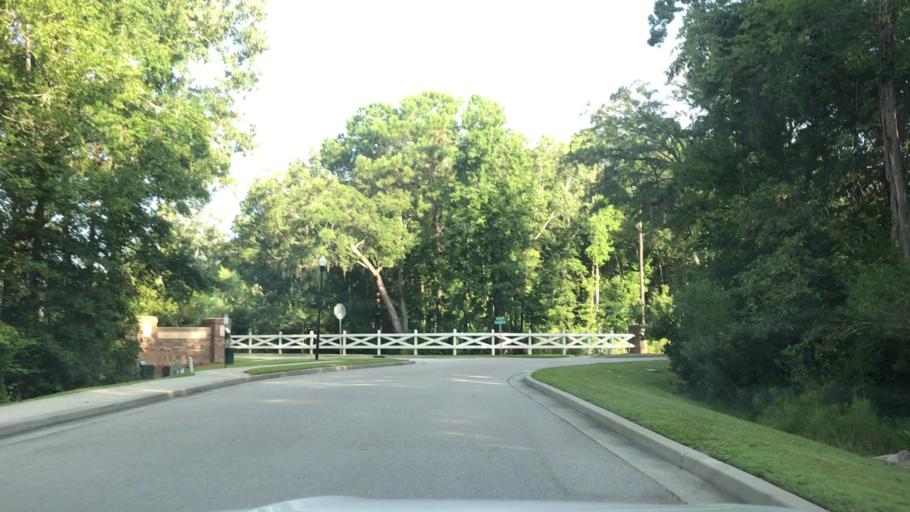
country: US
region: South Carolina
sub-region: Charleston County
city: Isle of Palms
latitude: 32.8908
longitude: -79.7497
